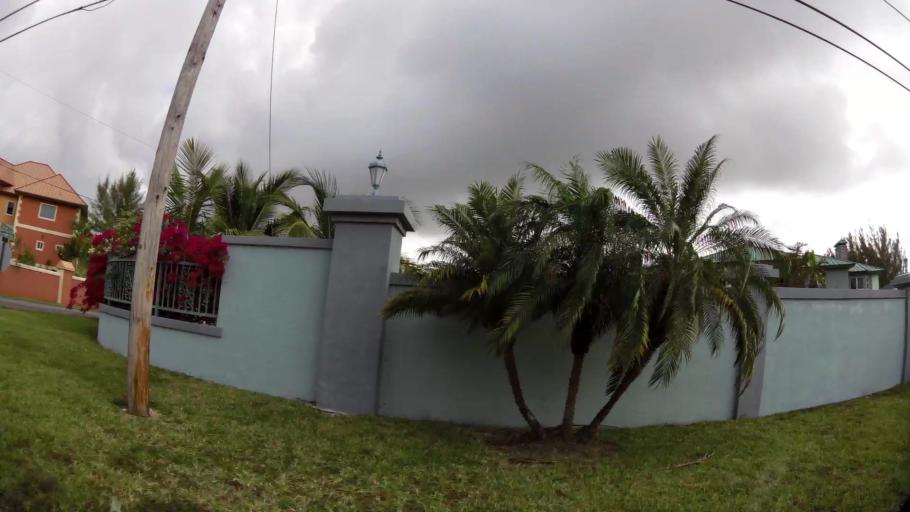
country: BS
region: Freeport
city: Lucaya
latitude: 26.5707
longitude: -78.5759
